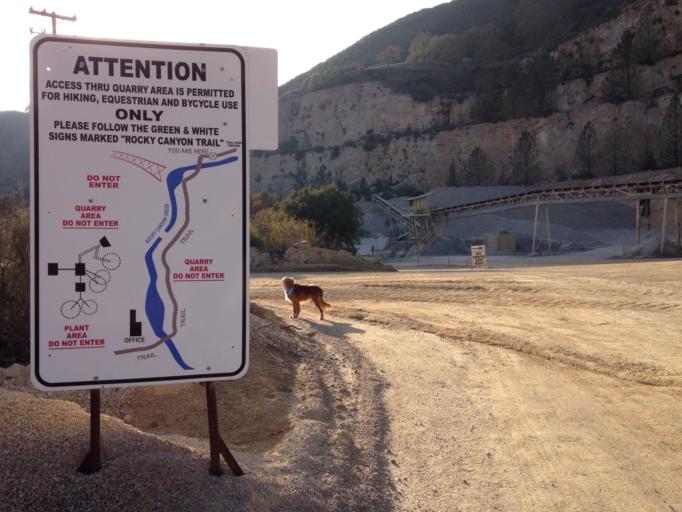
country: US
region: California
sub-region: San Luis Obispo County
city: Atascadero
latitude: 35.4744
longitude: -120.6114
